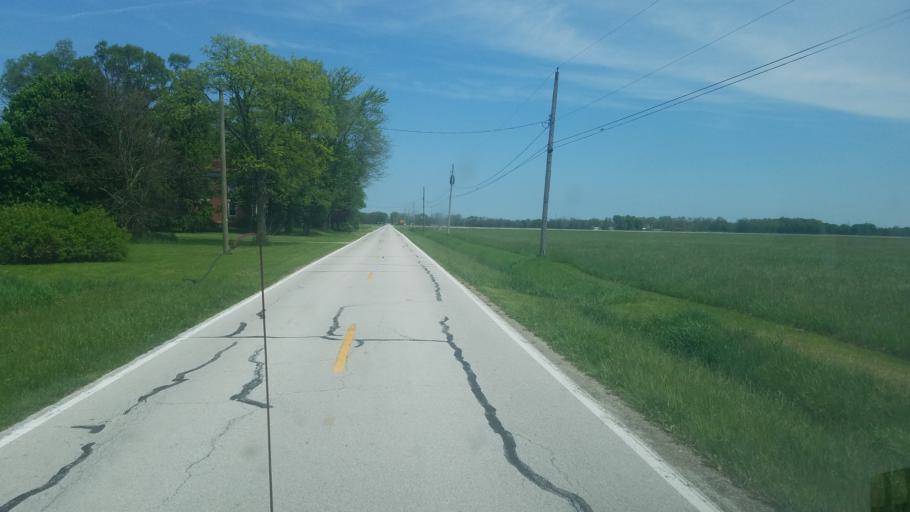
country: US
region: Ohio
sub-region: Sandusky County
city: Stony Prairie
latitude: 41.4110
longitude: -83.2020
